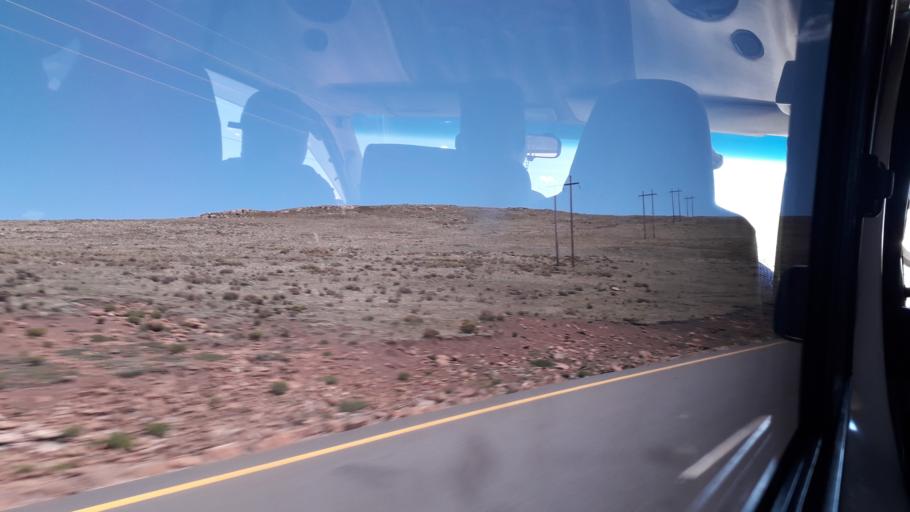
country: LS
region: Mokhotlong
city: Mokhotlong
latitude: -29.0624
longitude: 28.8500
